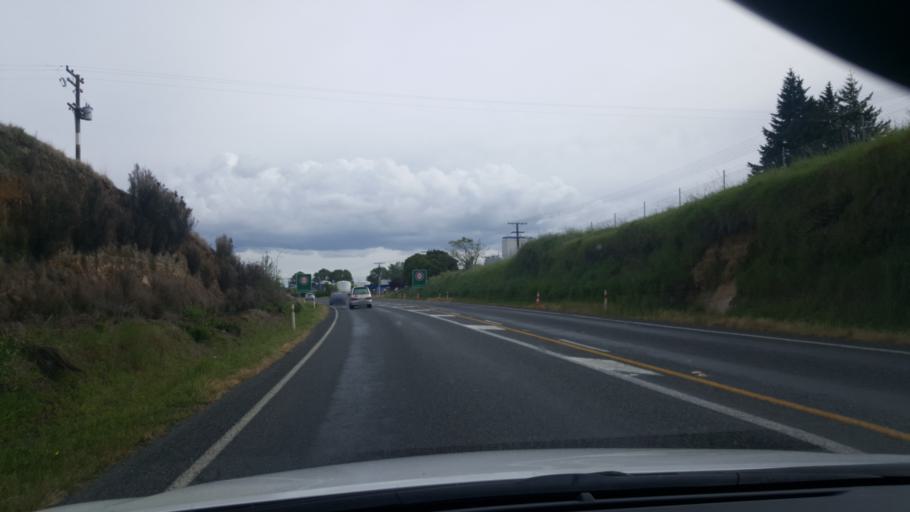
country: NZ
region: Bay of Plenty
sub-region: Rotorua District
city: Rotorua
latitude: -38.4223
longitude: 176.3172
